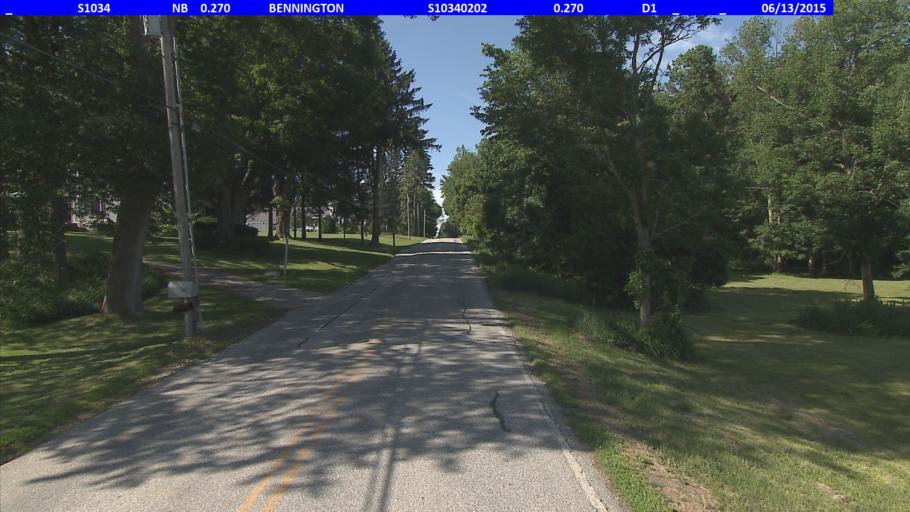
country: US
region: Vermont
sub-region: Bennington County
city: Bennington
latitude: 42.8560
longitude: -73.2063
